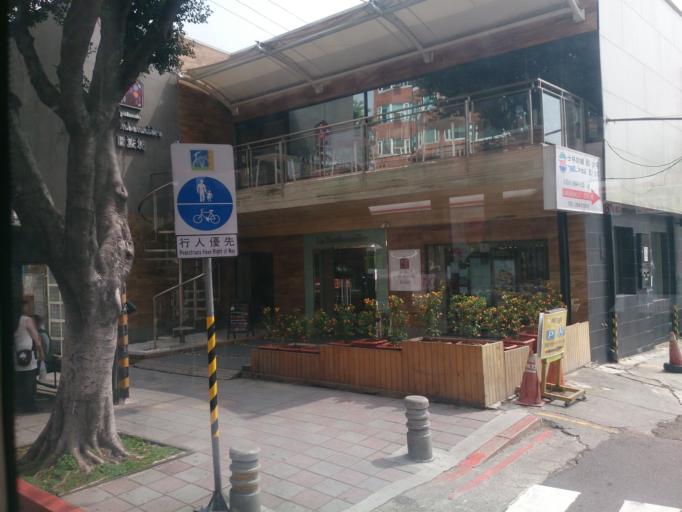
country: TW
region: Taipei
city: Taipei
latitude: 25.0959
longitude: 121.5288
